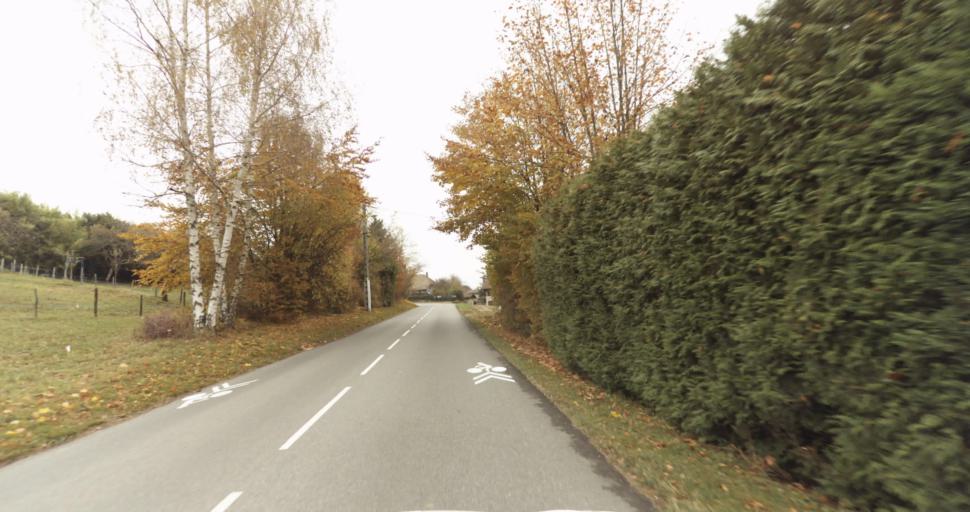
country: FR
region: Rhone-Alpes
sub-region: Departement de la Haute-Savoie
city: Cusy
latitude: 45.7763
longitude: 6.0197
